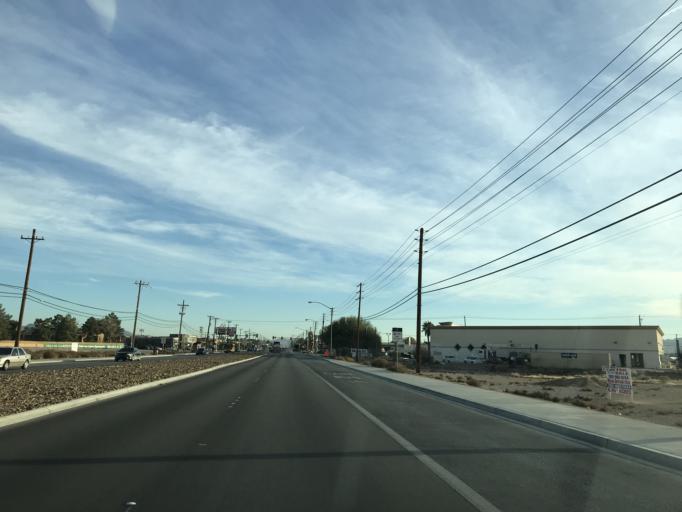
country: US
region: Nevada
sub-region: Clark County
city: Nellis Air Force Base
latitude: 36.2346
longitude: -115.0643
